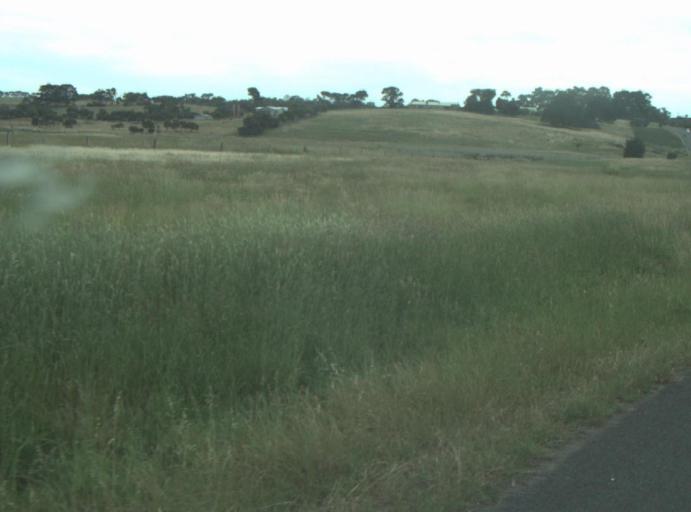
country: AU
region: Victoria
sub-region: Greater Geelong
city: Leopold
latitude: -38.2508
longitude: 144.5036
